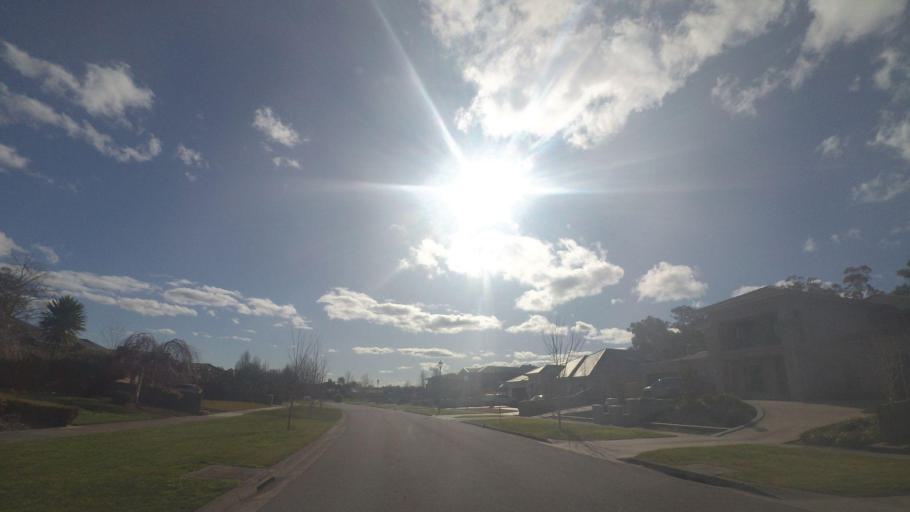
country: AU
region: Victoria
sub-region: Yarra Ranges
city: Lysterfield
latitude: -37.9200
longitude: 145.2907
